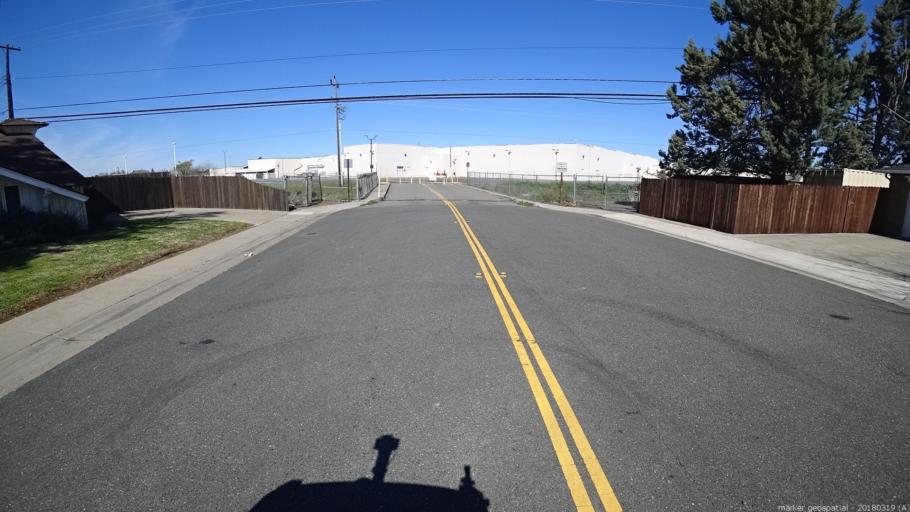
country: US
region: California
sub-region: Sacramento County
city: Parkway
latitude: 38.4933
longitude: -121.4532
